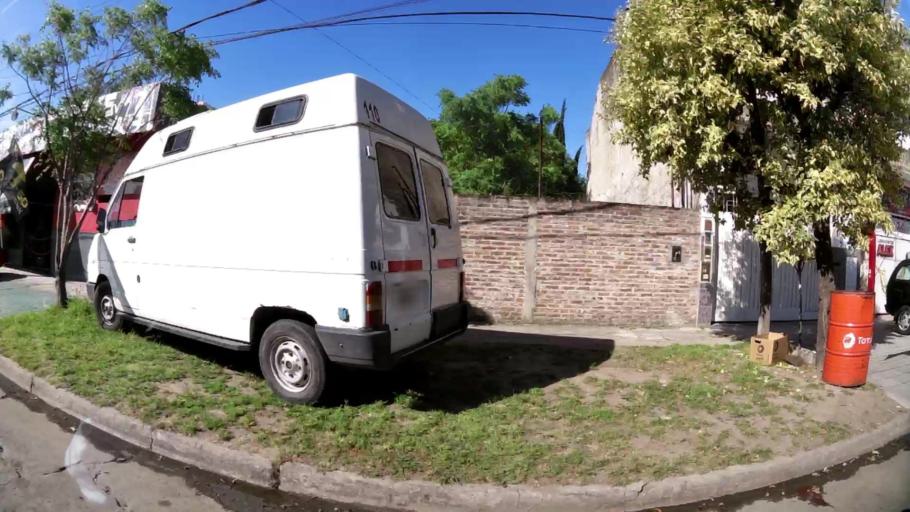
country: AR
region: Buenos Aires
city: Caseros
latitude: -34.5668
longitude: -58.5931
